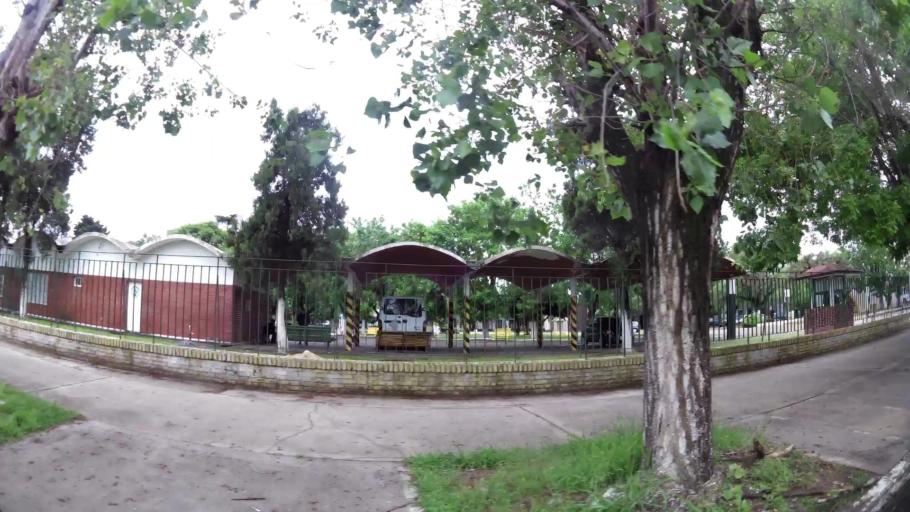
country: AR
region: Buenos Aires
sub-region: Partido de Lanus
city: Lanus
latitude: -34.7343
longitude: -58.3778
